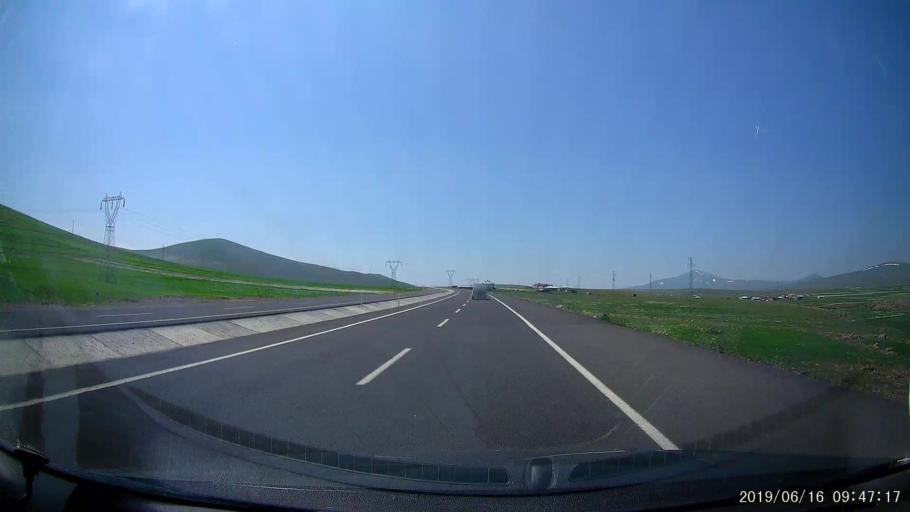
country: TR
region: Kars
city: Digor
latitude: 40.4504
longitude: 43.3424
